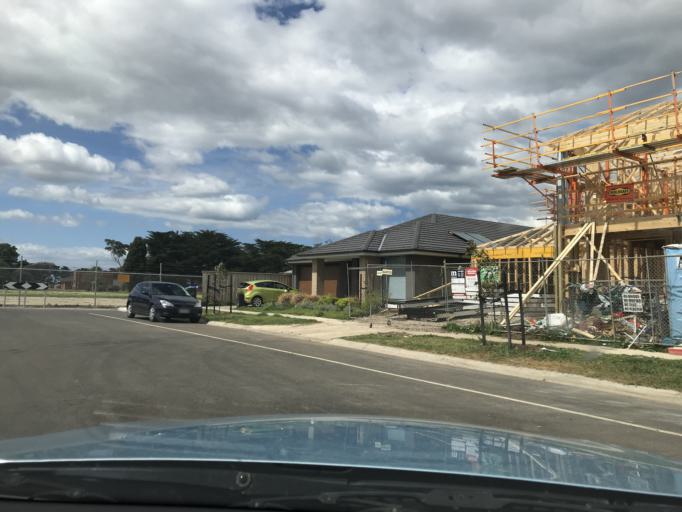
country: AU
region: Victoria
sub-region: Wyndham
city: Williams Landing
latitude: -37.8612
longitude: 144.7561
